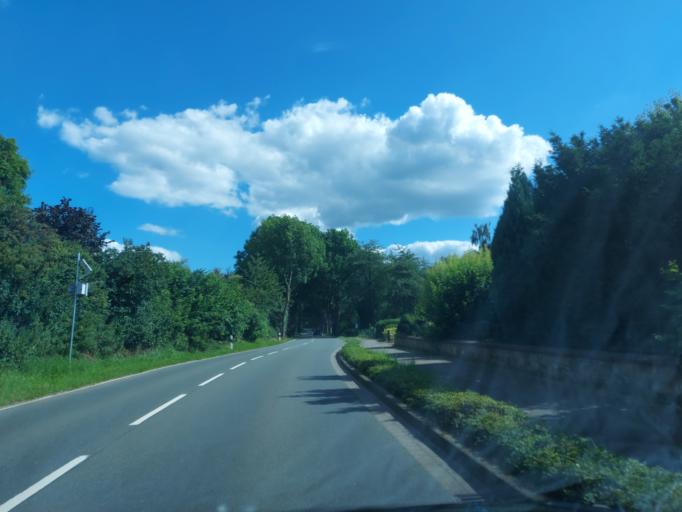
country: DE
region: Lower Saxony
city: Hagen
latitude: 52.1929
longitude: 7.9778
